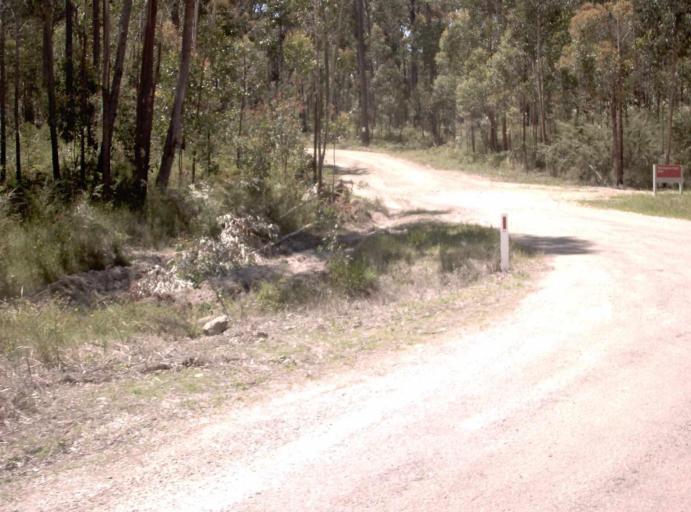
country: AU
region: Victoria
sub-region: East Gippsland
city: Lakes Entrance
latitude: -37.6878
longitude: 148.7513
